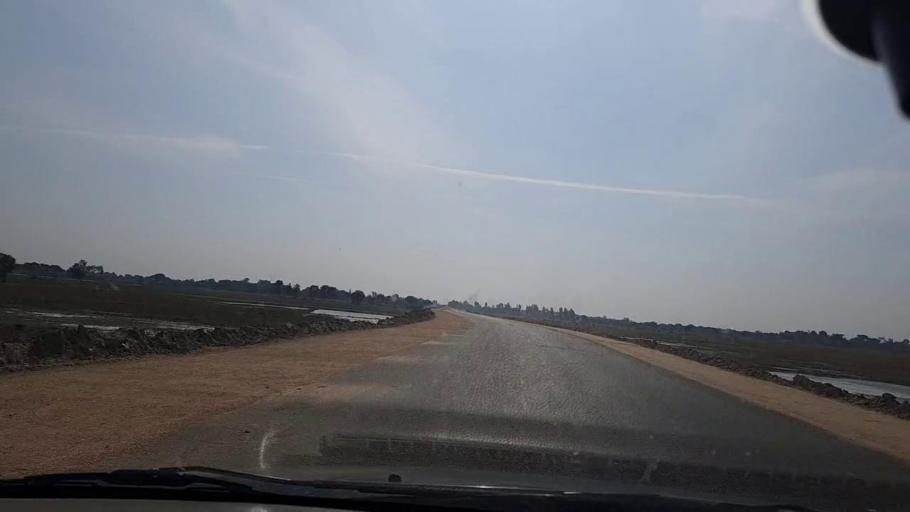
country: PK
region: Sindh
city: Mirpur Batoro
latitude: 24.7420
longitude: 68.2740
